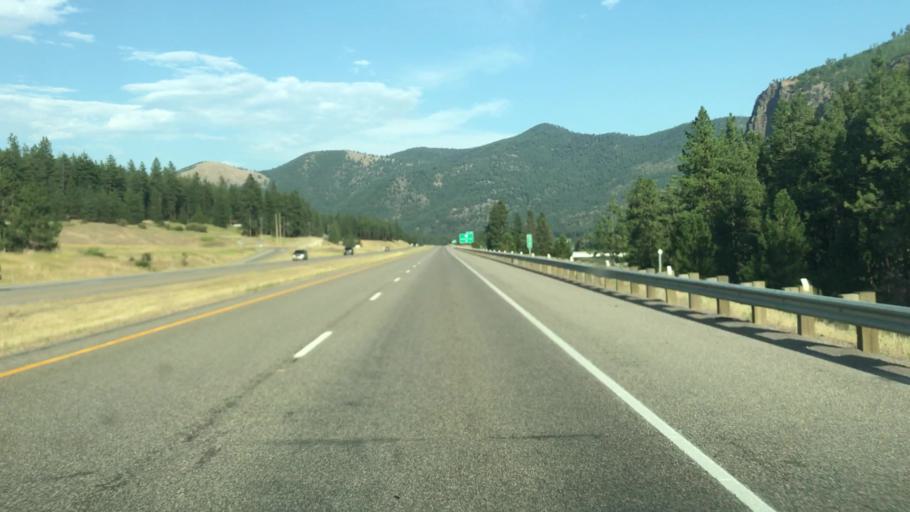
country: US
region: Montana
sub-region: Missoula County
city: Frenchtown
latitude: 46.9955
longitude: -114.4560
